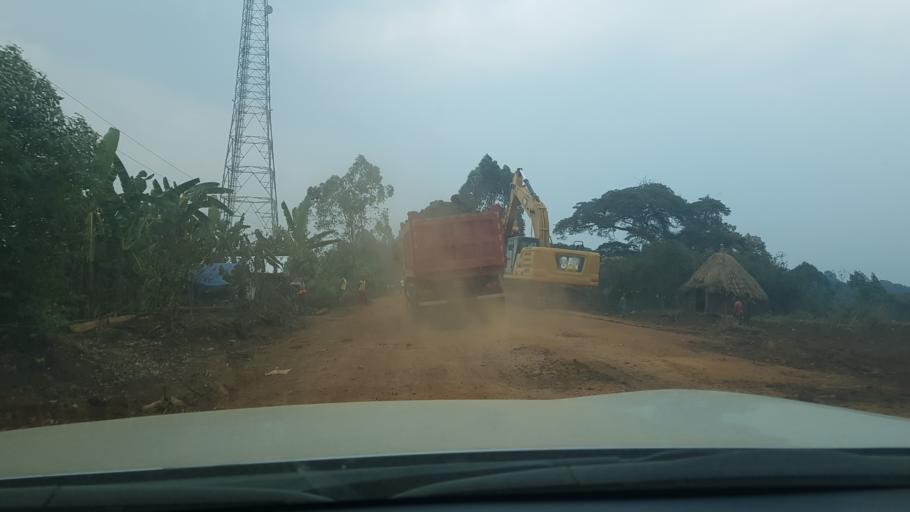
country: ET
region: Oromiya
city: Gore
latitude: 7.8985
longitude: 35.4950
